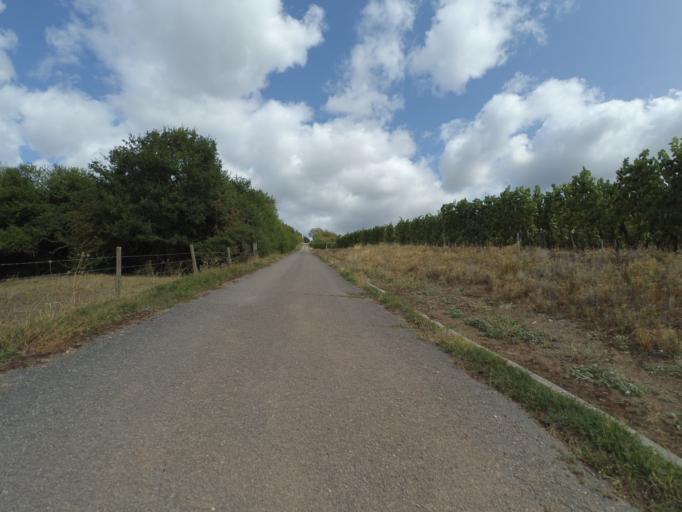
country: LU
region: Grevenmacher
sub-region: Canton de Remich
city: Lenningen
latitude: 49.6056
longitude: 6.3769
